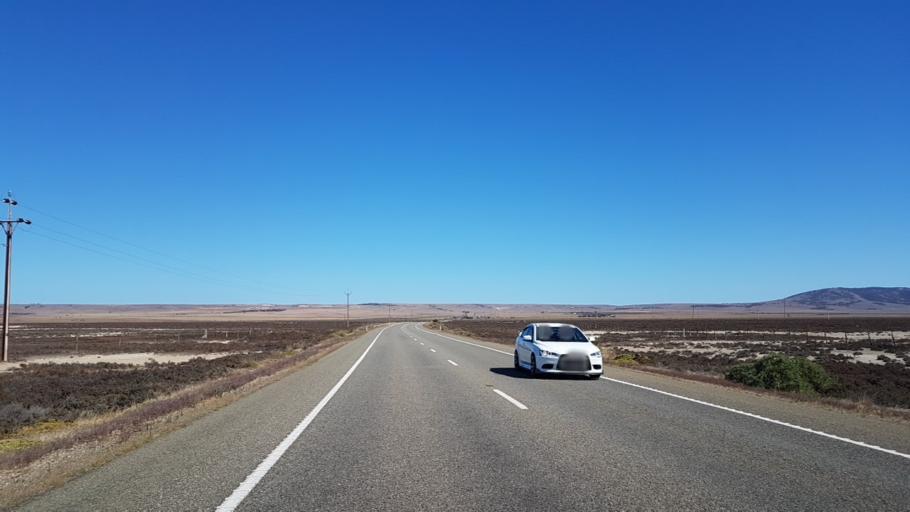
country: AU
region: South Australia
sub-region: Wakefield
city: Balaklava
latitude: -34.1023
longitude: 138.1087
